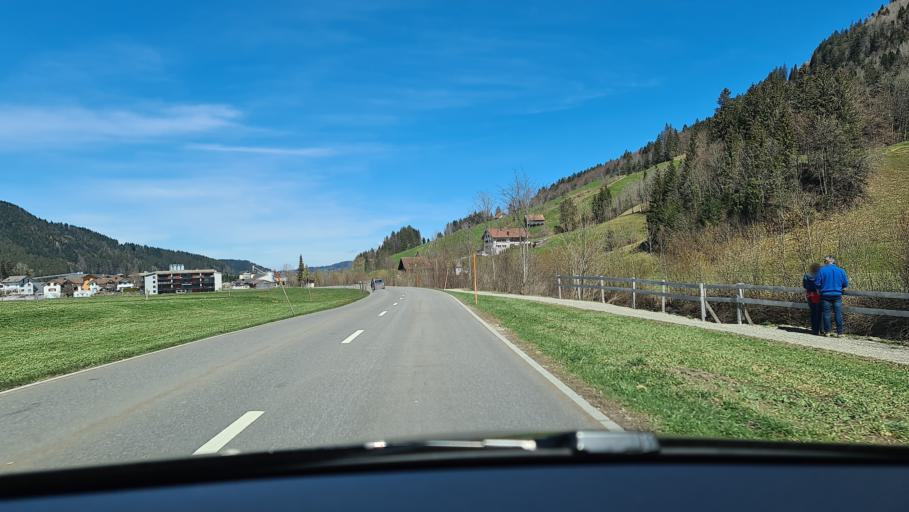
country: CH
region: Schwyz
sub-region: Bezirk Einsiedeln
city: Einsiedeln
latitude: 47.0954
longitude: 8.7271
